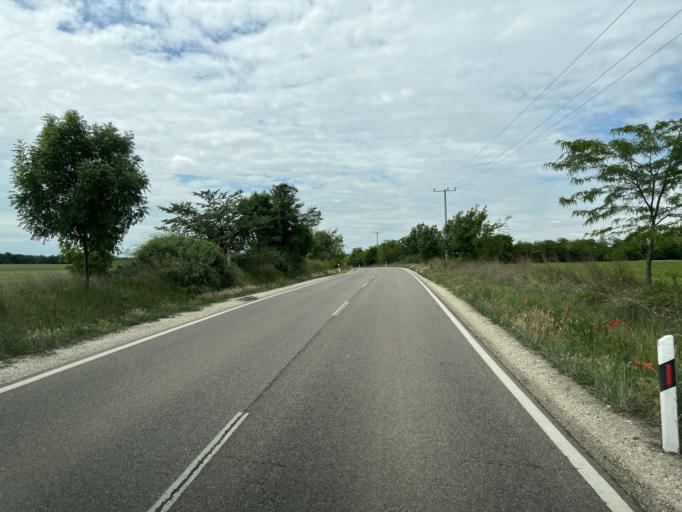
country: HU
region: Pest
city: Koka
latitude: 47.5018
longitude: 19.5899
